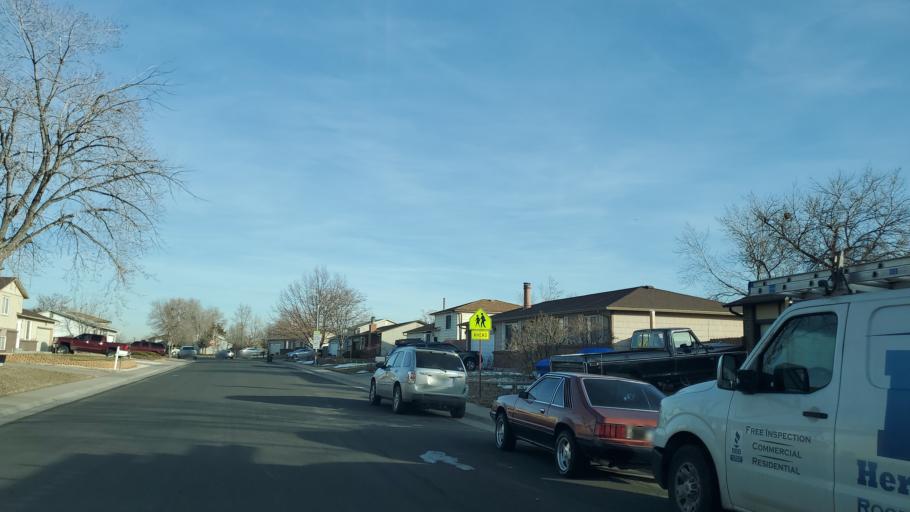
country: US
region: Colorado
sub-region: Adams County
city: Northglenn
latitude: 39.9089
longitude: -104.9480
